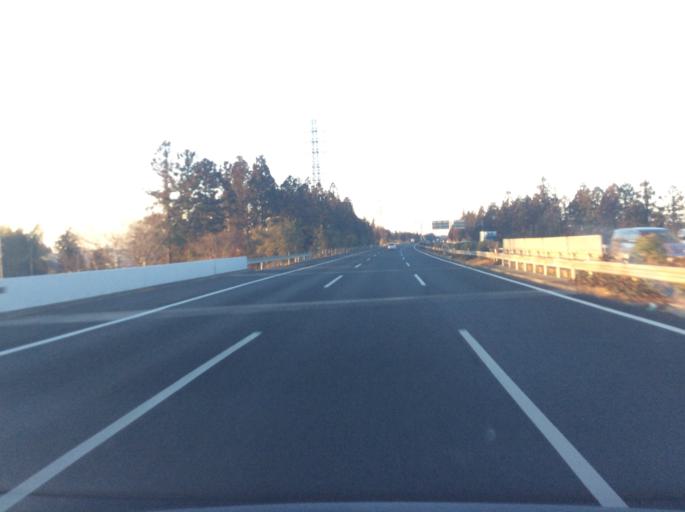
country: JP
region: Ibaraki
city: Mito-shi
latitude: 36.3698
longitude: 140.3828
